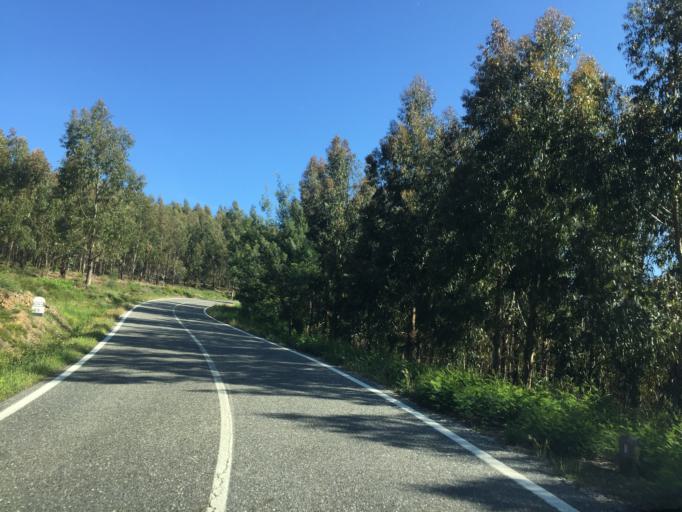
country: PT
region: Coimbra
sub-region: Pampilhosa da Serra
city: Pampilhosa da Serra
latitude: 40.0505
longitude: -7.8672
